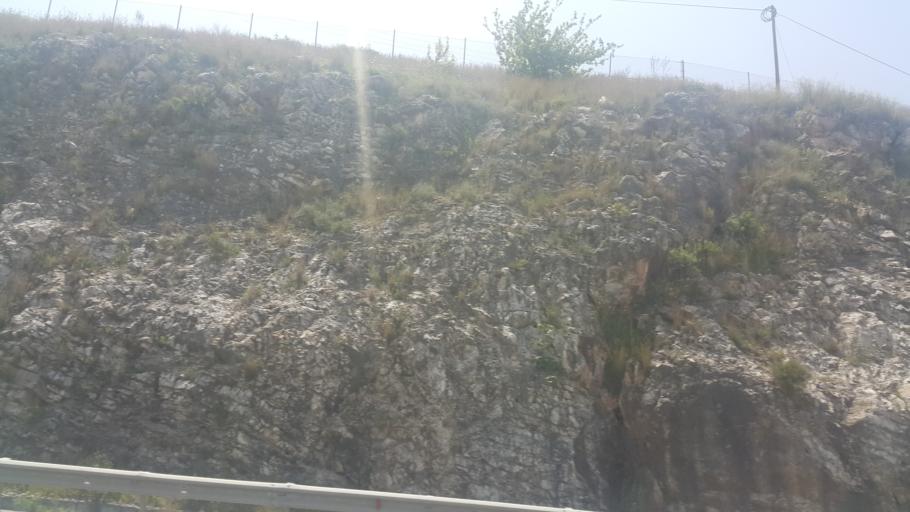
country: TR
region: Hatay
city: Iskenderun
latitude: 36.5646
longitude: 36.1794
